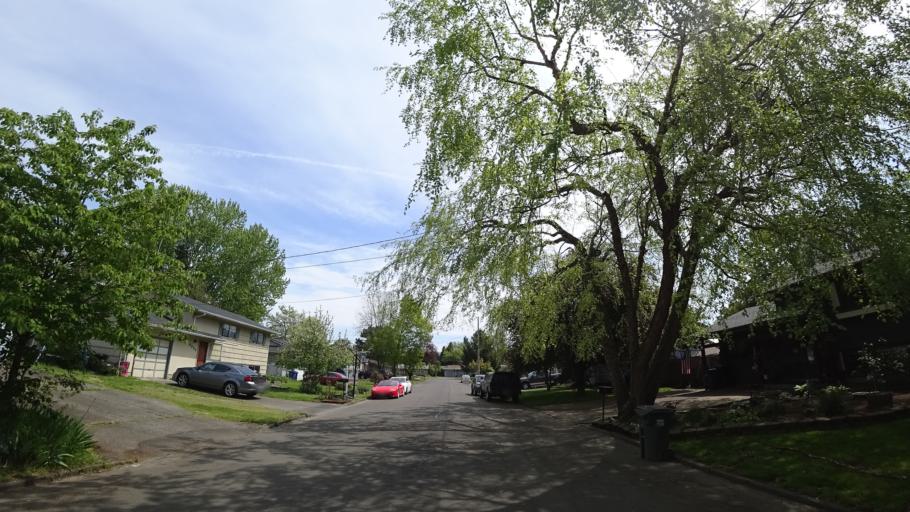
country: US
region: Oregon
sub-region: Clackamas County
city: Milwaukie
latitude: 45.4549
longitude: -122.6103
